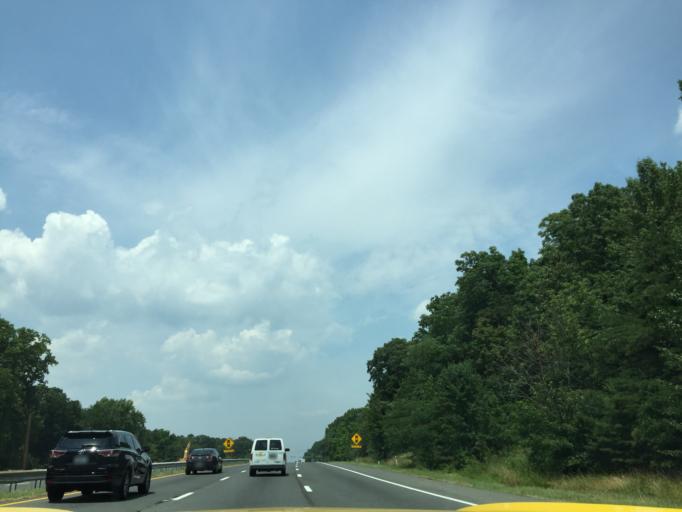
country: US
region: Maryland
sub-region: Prince George's County
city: Fort Washington
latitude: 38.7084
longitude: -76.9898
